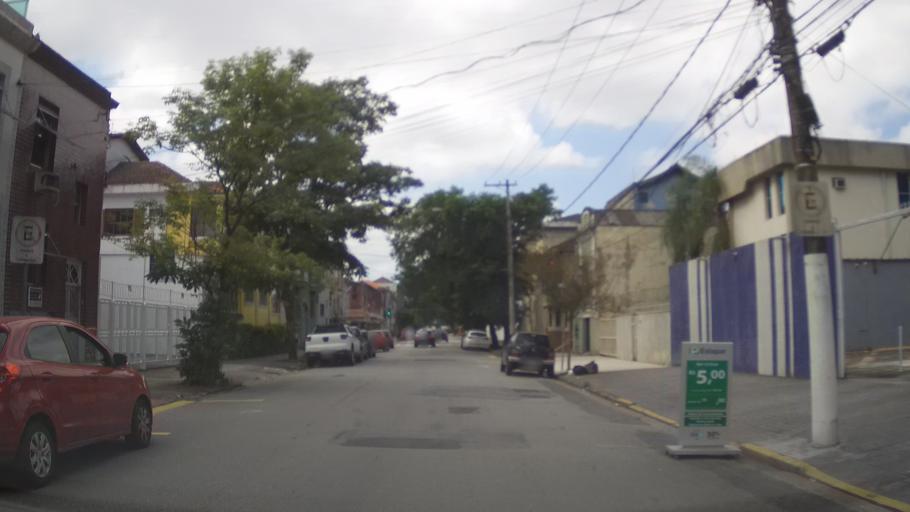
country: BR
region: Sao Paulo
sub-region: Santos
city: Santos
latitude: -23.9492
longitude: -46.3216
